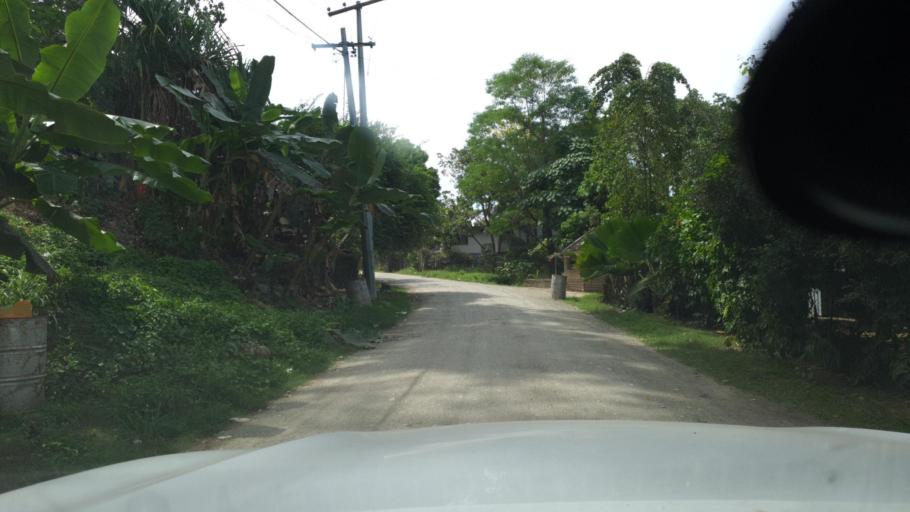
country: SB
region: Guadalcanal
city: Honiara
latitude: -9.4270
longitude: 159.9204
